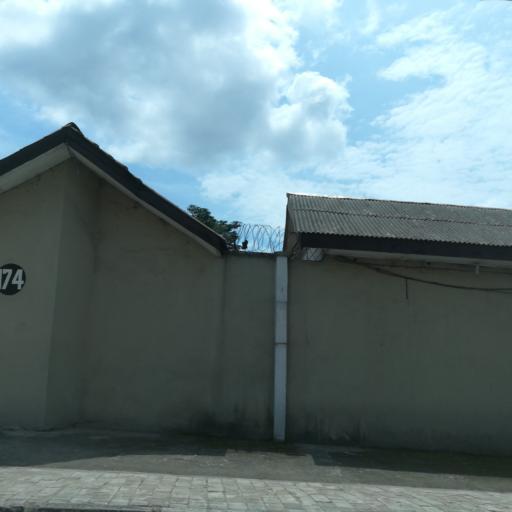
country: NG
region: Rivers
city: Port Harcourt
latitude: 4.7817
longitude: 7.0417
